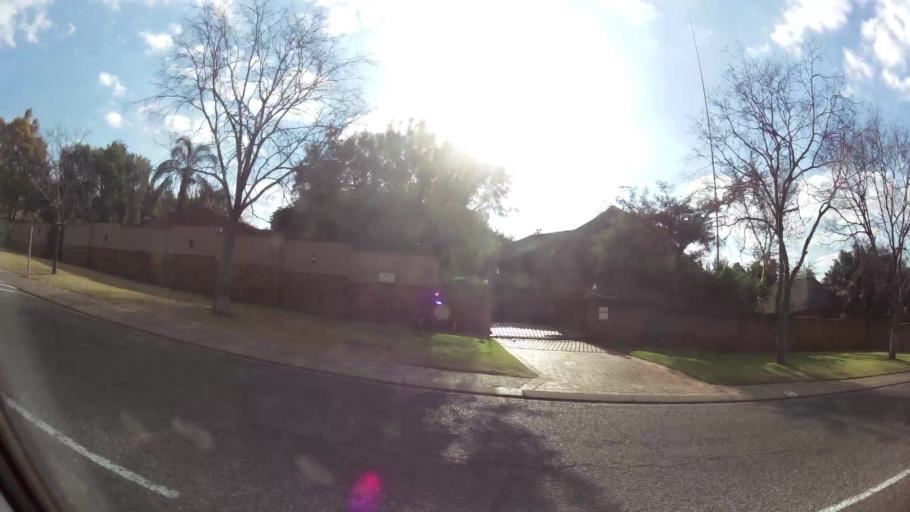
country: ZA
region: Gauteng
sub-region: City of Johannesburg Metropolitan Municipality
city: Diepsloot
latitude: -26.0091
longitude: 28.0236
